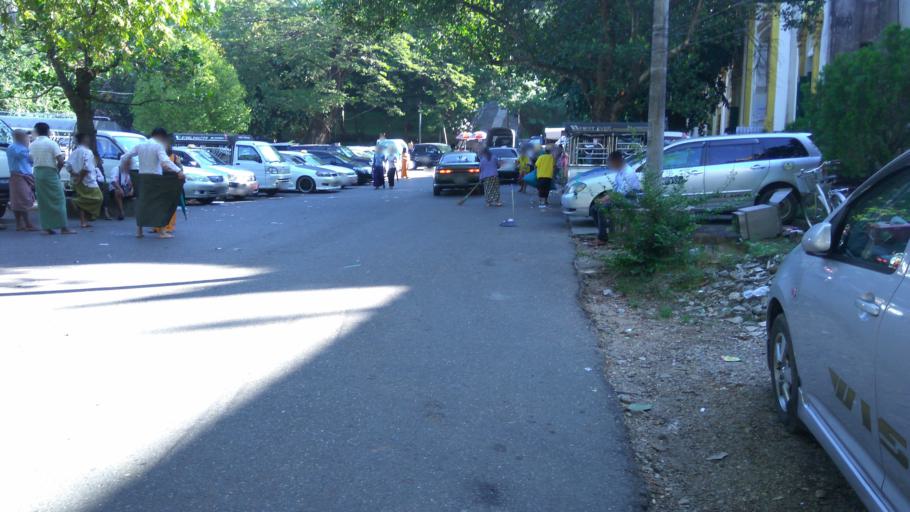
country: MM
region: Yangon
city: Yangon
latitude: 16.7979
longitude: 96.1473
